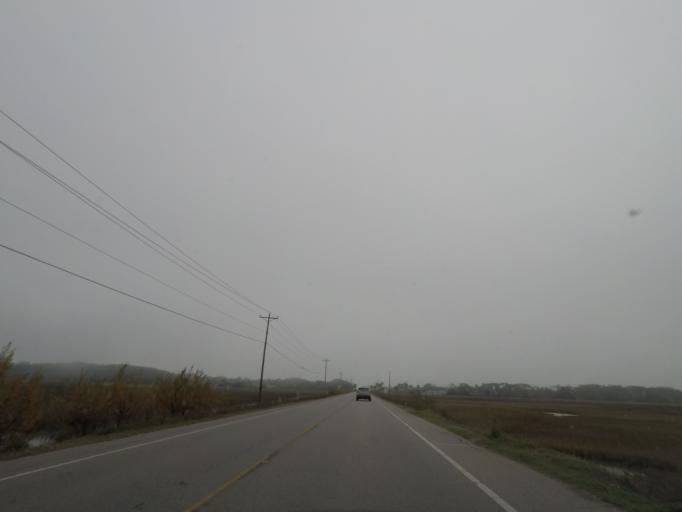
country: US
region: South Carolina
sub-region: Charleston County
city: Seabrook Island
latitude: 32.5073
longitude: -80.2988
